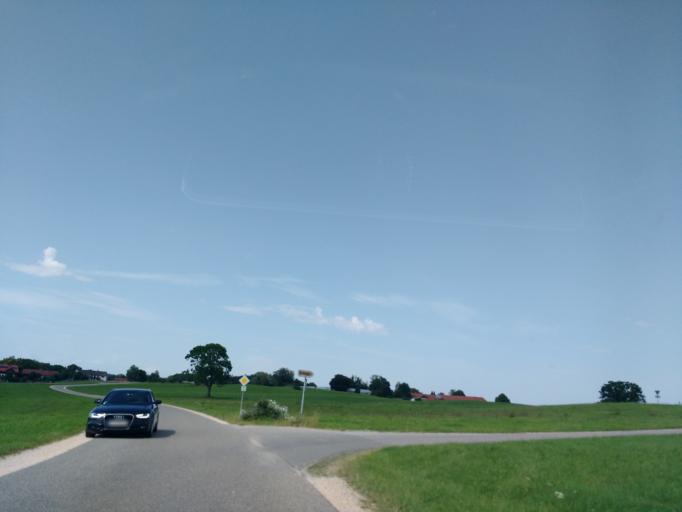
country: DE
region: Bavaria
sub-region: Upper Bavaria
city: Obing
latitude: 48.0097
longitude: 12.4407
